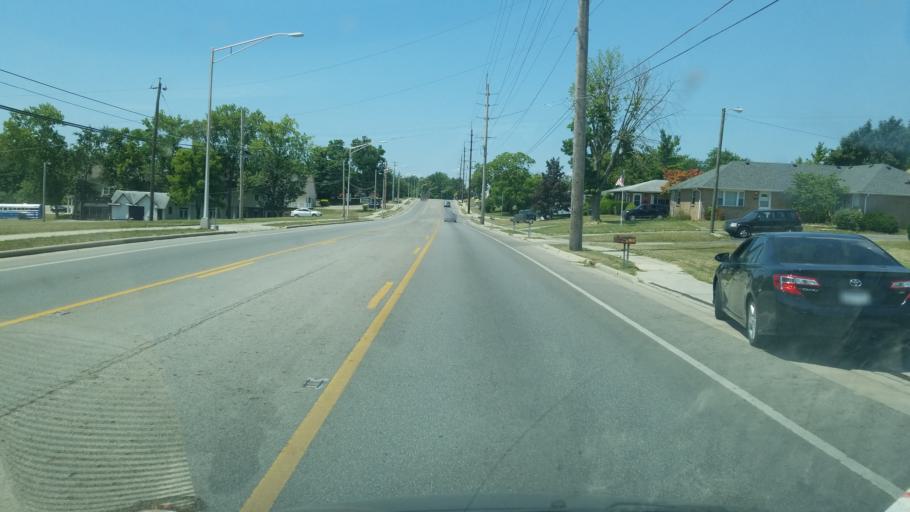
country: US
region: Ohio
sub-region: Franklin County
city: Lincoln Village
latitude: 39.9281
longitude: -83.0932
